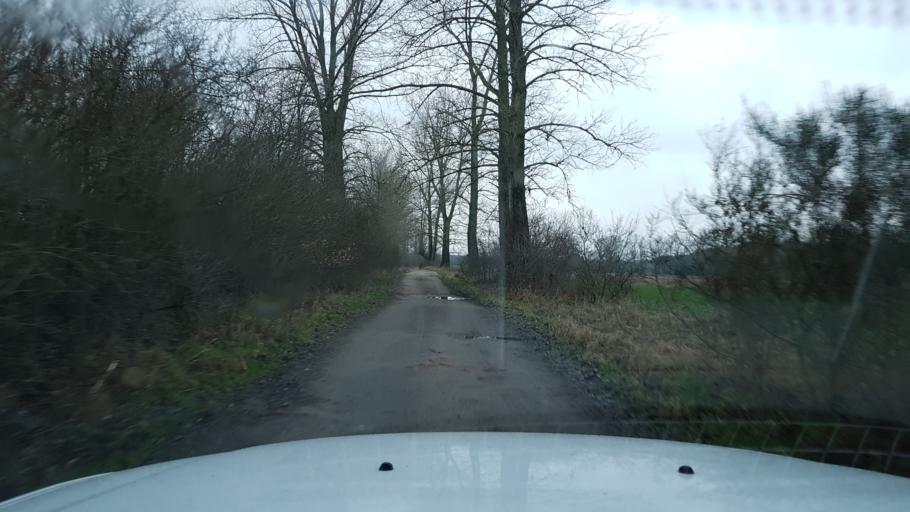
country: PL
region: West Pomeranian Voivodeship
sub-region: Powiat gryficki
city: Brojce
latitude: 53.9835
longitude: 15.3101
